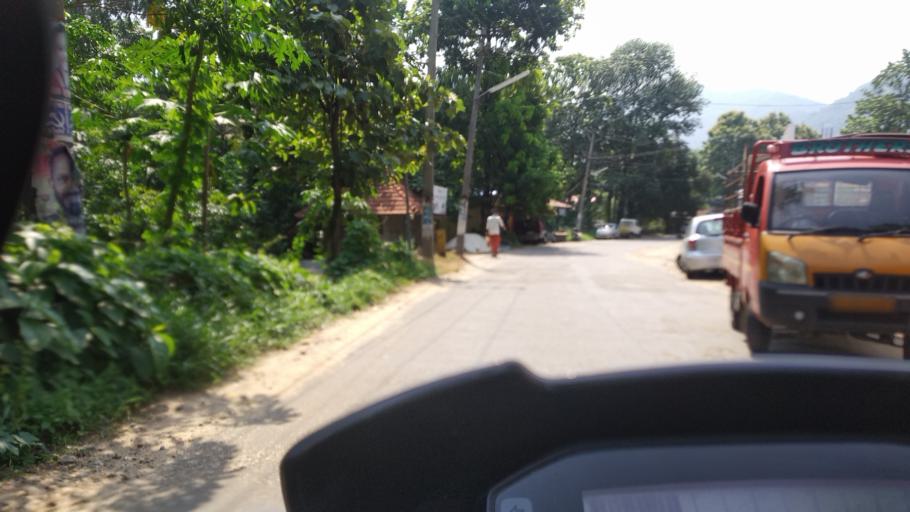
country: IN
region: Kerala
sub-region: Kottayam
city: Erattupetta
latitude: 9.6991
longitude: 76.8193
